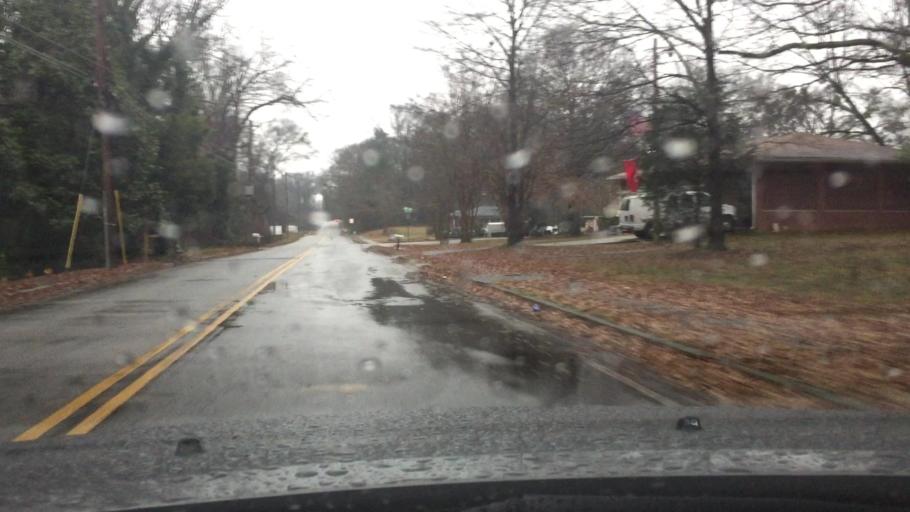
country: US
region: Georgia
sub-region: Cobb County
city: Fair Oaks
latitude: 33.9111
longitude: -84.5399
